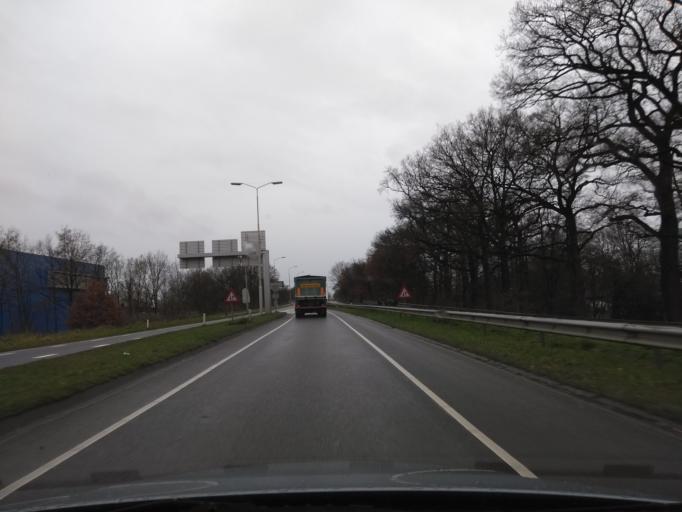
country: NL
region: Overijssel
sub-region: Gemeente Wierden
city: Wierden
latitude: 52.3560
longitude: 6.6228
